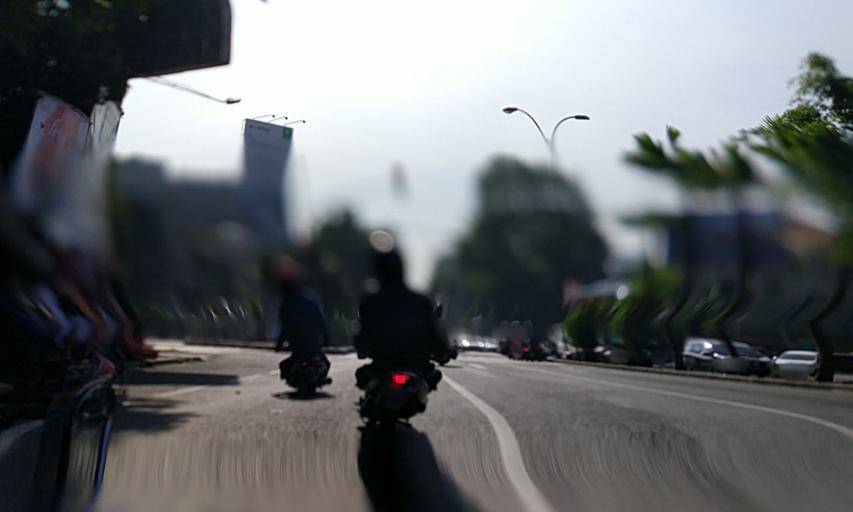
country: ID
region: West Java
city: Bandung
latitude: -6.9159
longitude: 107.6295
